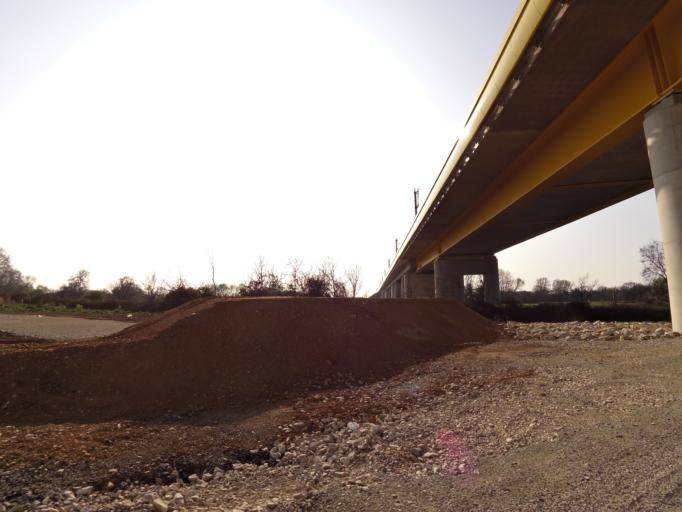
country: FR
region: Languedoc-Roussillon
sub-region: Departement du Gard
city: Vestric-et-Candiac
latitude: 43.7234
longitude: 4.2657
